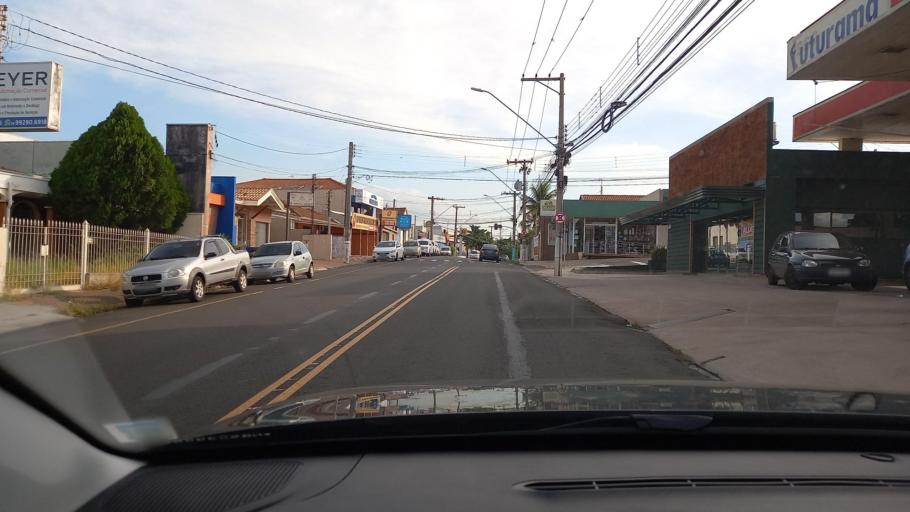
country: BR
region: Sao Paulo
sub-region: Mogi-Mirim
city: Mogi Mirim
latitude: -22.4398
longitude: -46.9656
